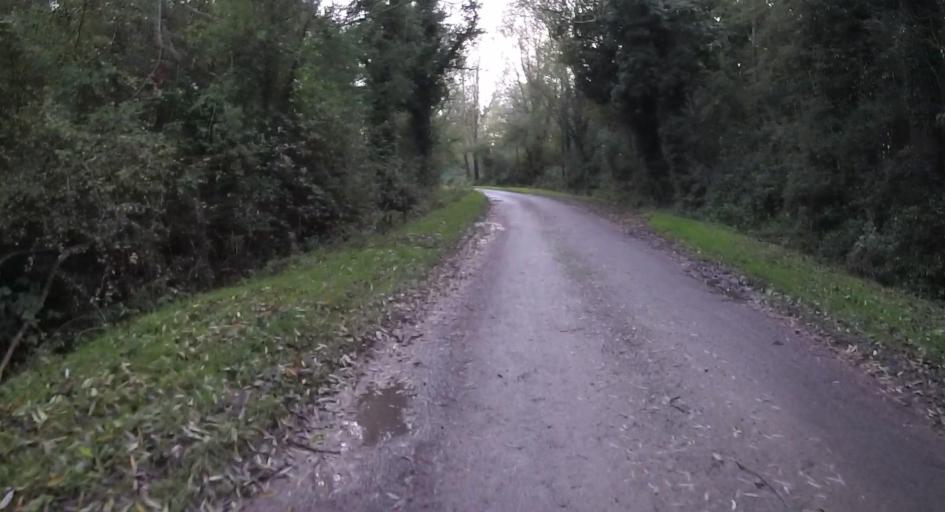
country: GB
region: England
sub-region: Wokingham
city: Swallowfield
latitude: 51.3745
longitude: -0.9611
